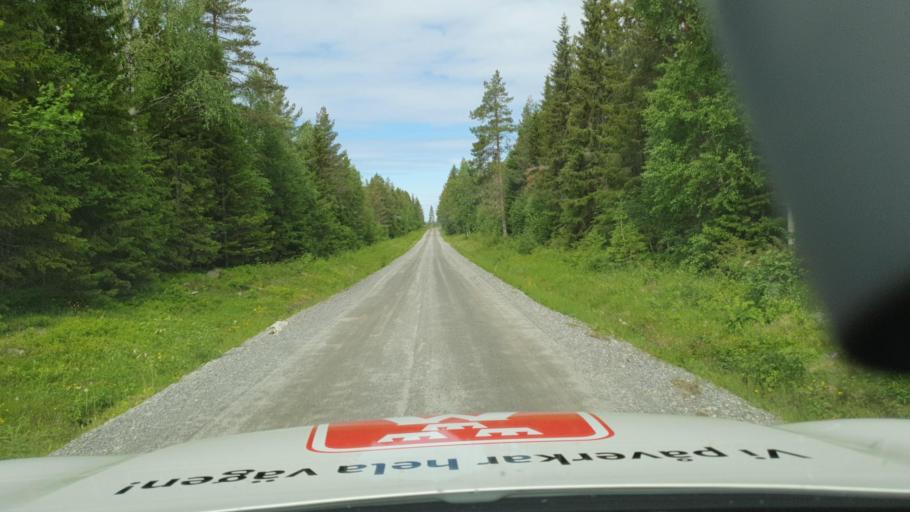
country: SE
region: Vaesterbotten
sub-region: Skelleftea Kommun
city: Langsele
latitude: 64.6257
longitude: 20.2554
